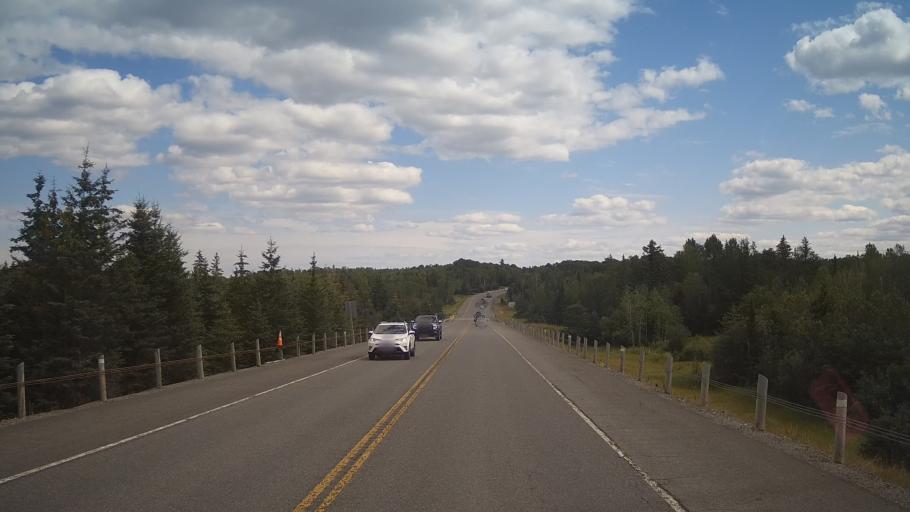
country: CA
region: Ontario
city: Greater Sudbury
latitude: 46.4931
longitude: -80.5579
